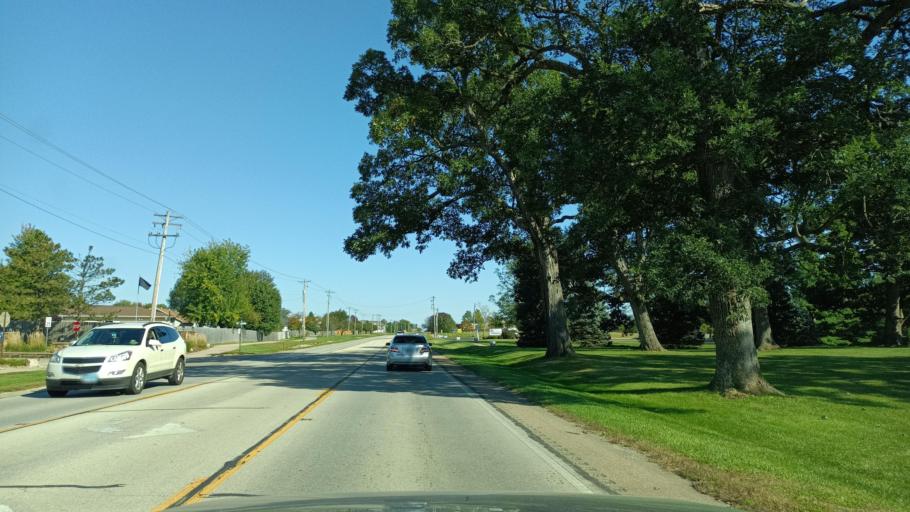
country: US
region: Illinois
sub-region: Champaign County
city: Mahomet
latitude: 40.1874
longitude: -88.3870
